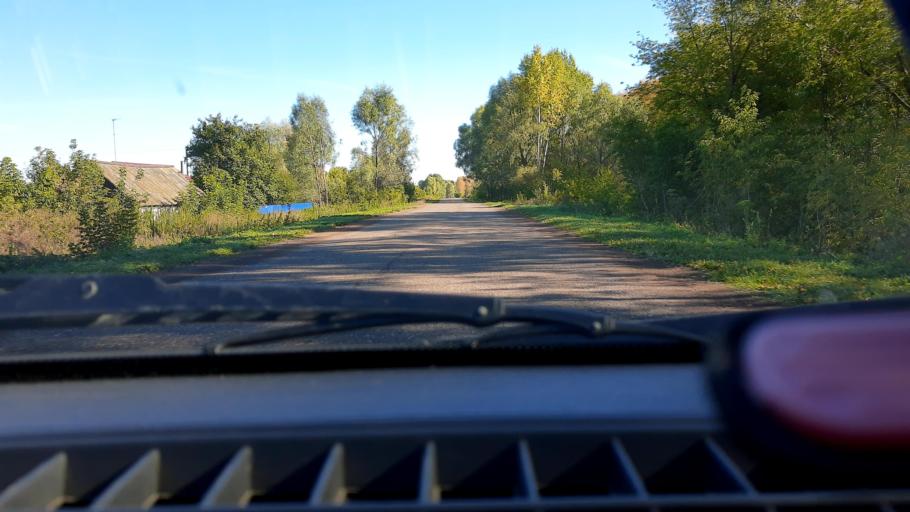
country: RU
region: Bashkortostan
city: Kushnarenkovo
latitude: 55.1008
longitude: 55.5115
